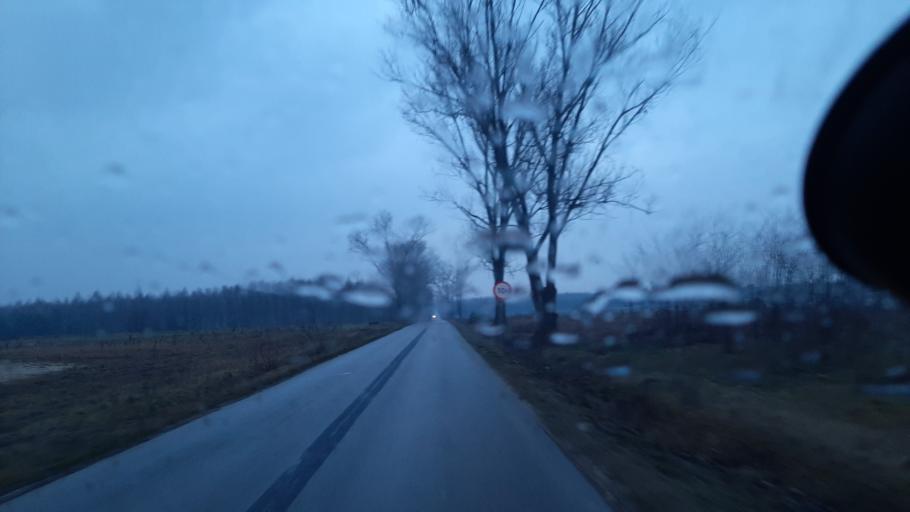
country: PL
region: Lublin Voivodeship
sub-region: Powiat lubartowski
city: Lubartow
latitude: 51.5101
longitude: 22.5908
